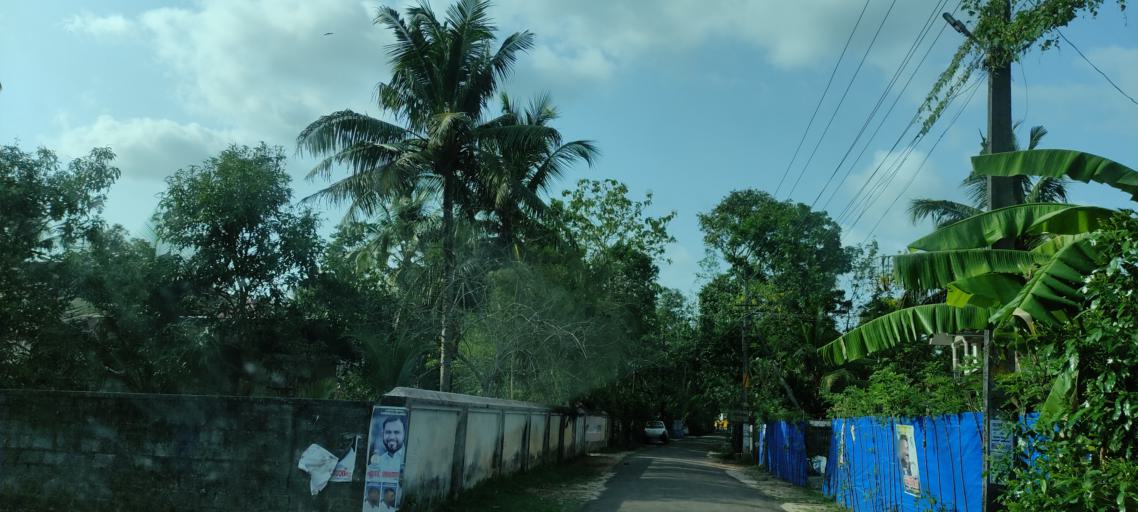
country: IN
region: Kerala
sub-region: Alappuzha
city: Vayalar
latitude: 9.6839
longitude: 76.3254
